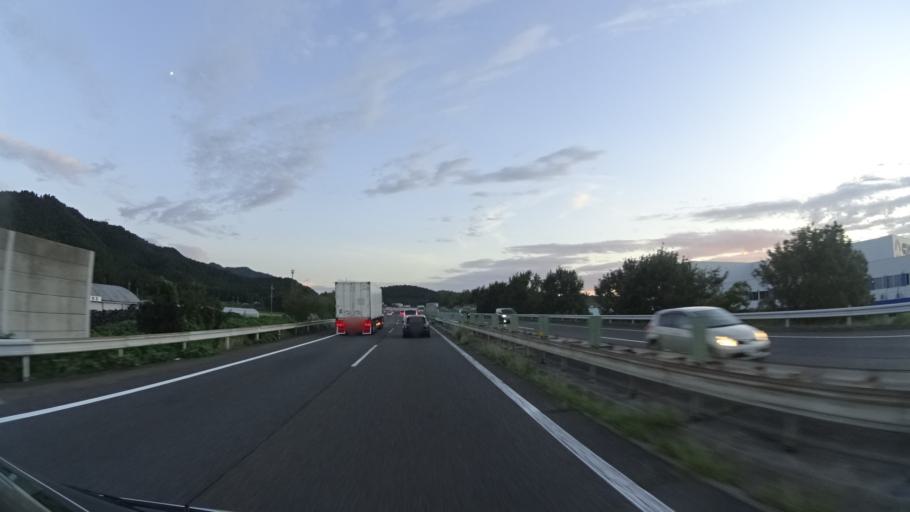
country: JP
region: Shiga Prefecture
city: Hikone
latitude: 35.1972
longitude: 136.2823
